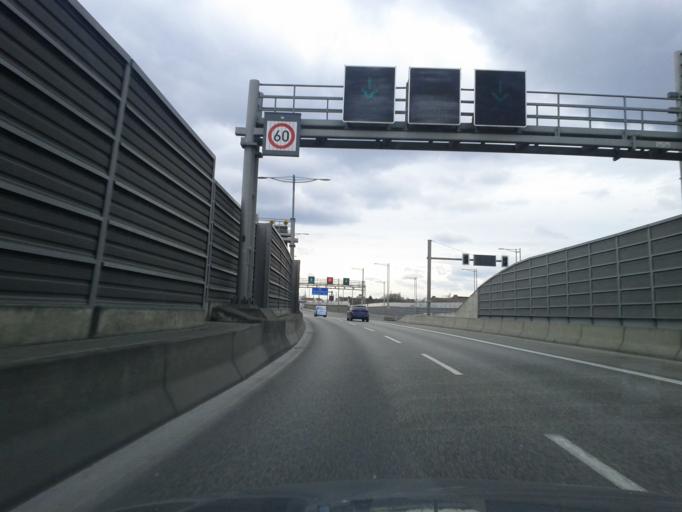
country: DE
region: Berlin
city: Treptow Bezirk
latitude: 52.4634
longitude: 13.4512
